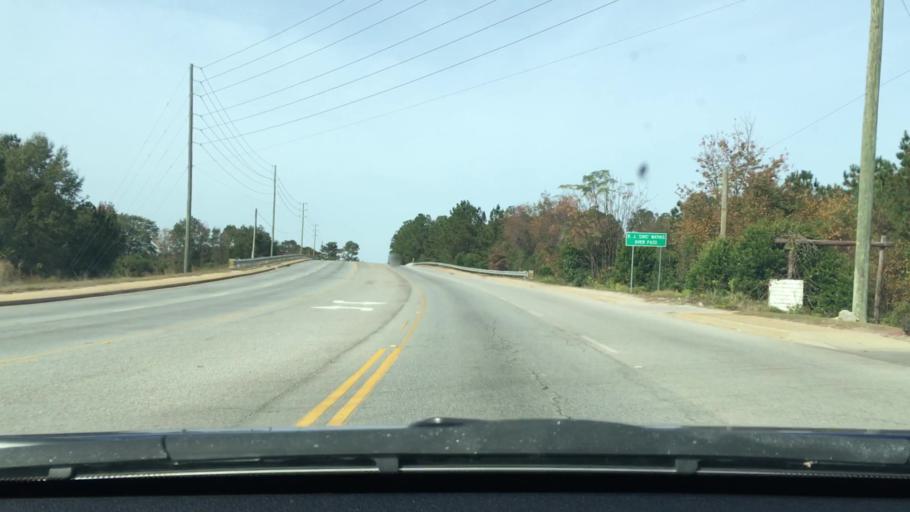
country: US
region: South Carolina
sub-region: Sumter County
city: South Sumter
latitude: 33.9069
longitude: -80.3797
